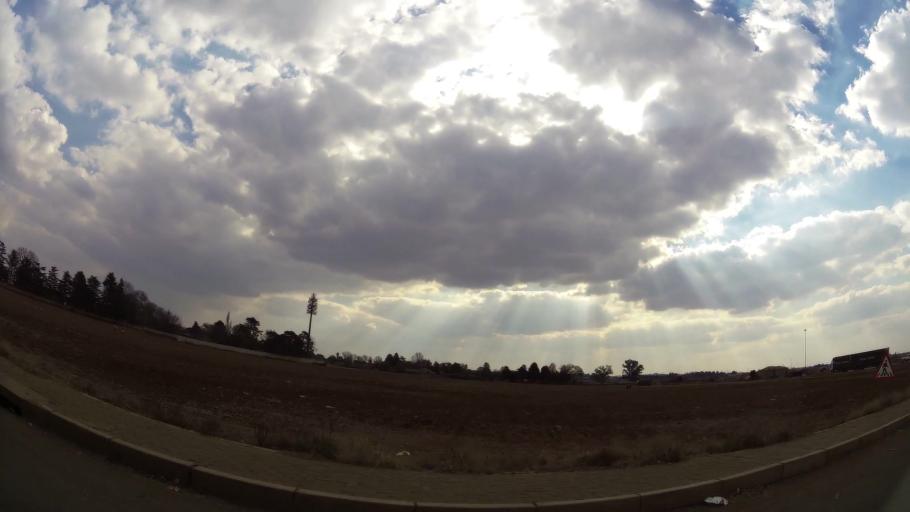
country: ZA
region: Mpumalanga
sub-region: Nkangala District Municipality
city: Delmas
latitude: -26.1476
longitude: 28.6907
